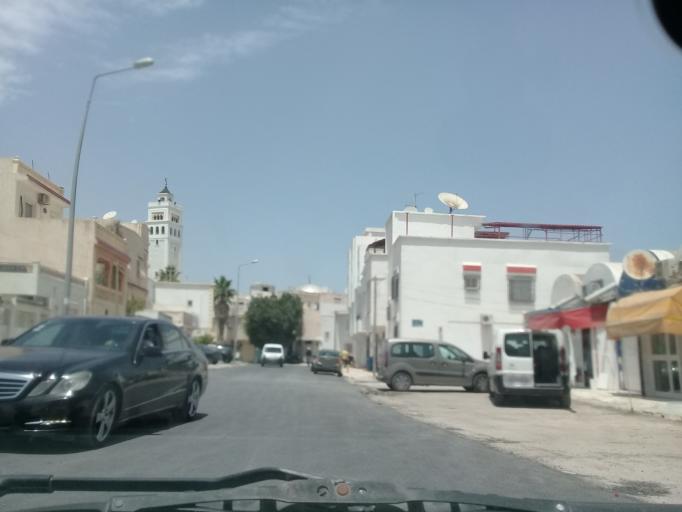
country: TN
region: Ariana
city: Ariana
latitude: 36.8331
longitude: 10.1993
